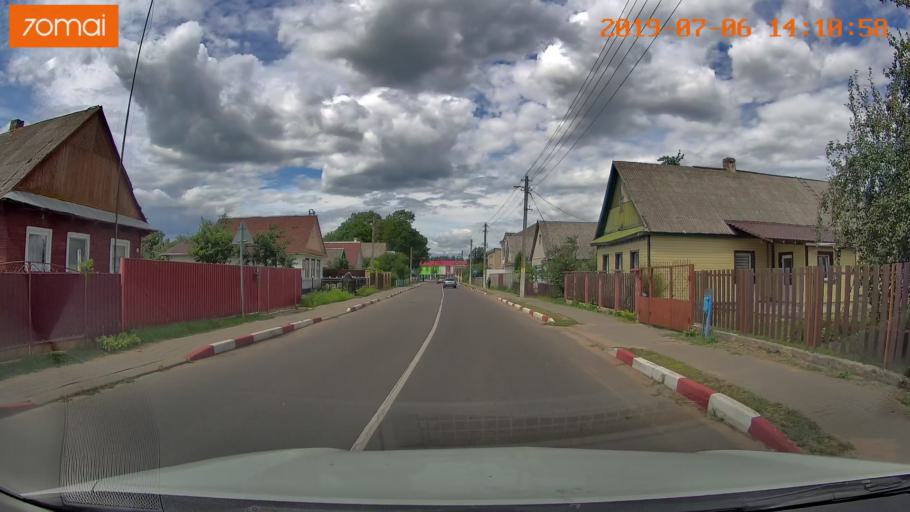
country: BY
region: Minsk
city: Ivyanyets
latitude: 53.8873
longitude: 26.7426
